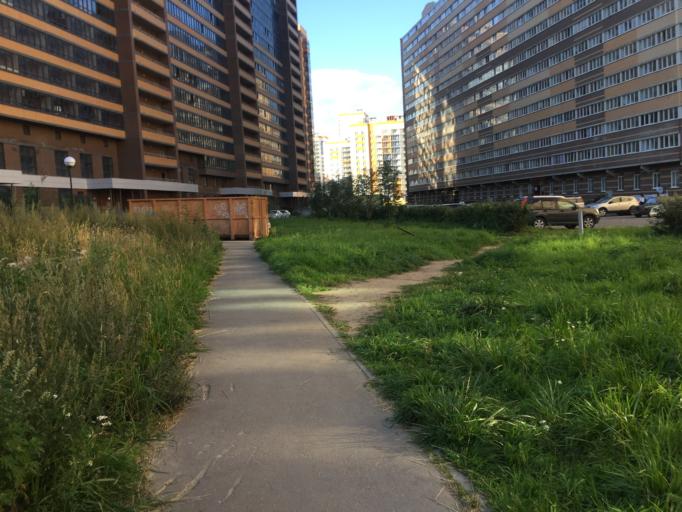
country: RU
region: Leningrad
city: Murino
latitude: 60.0554
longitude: 30.4308
